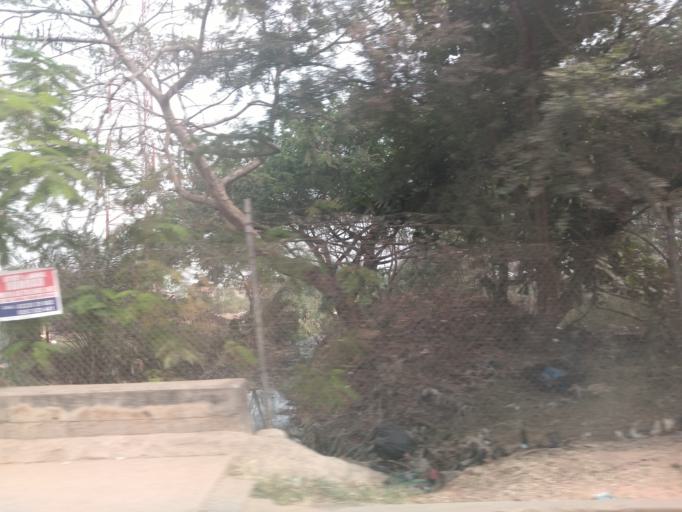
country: GH
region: Ashanti
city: Kumasi
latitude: 6.7090
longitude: -1.6169
